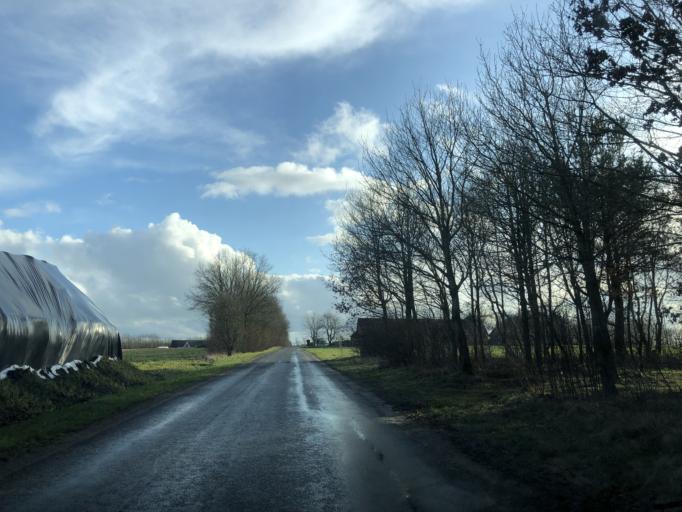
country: DK
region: North Denmark
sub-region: Vesthimmerland Kommune
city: Alestrup
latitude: 56.6403
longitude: 9.6151
